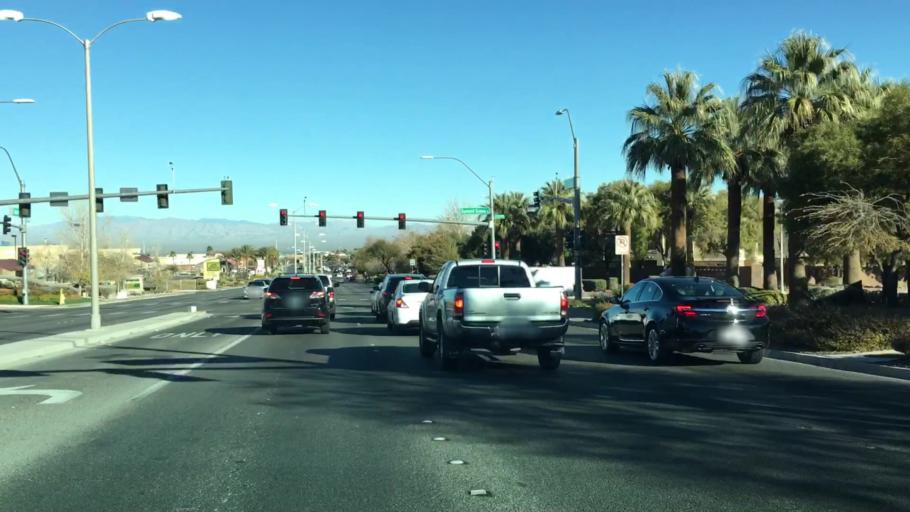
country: US
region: Nevada
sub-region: Clark County
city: Whitney
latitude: 35.9881
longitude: -115.1009
